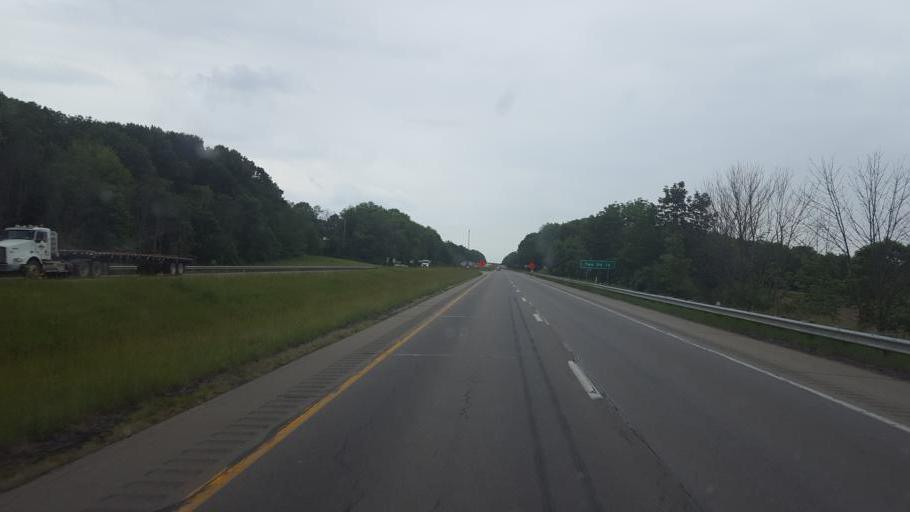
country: US
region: Ohio
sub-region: Wayne County
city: Shreve
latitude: 40.7844
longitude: -82.1147
